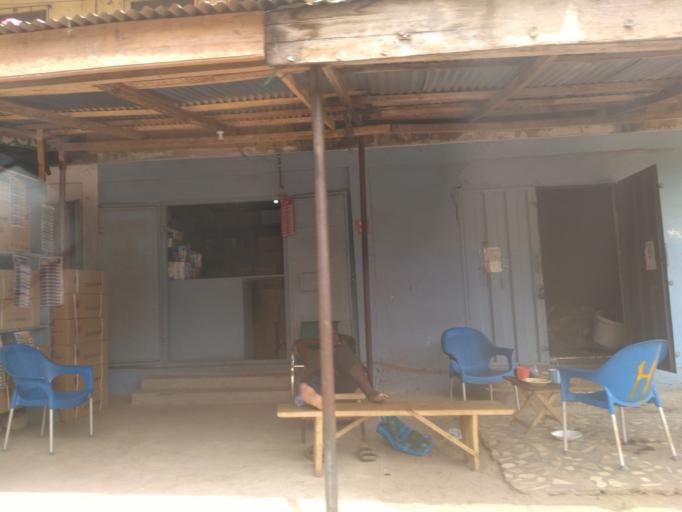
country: GH
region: Ashanti
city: Kumasi
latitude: 6.7017
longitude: -1.6146
